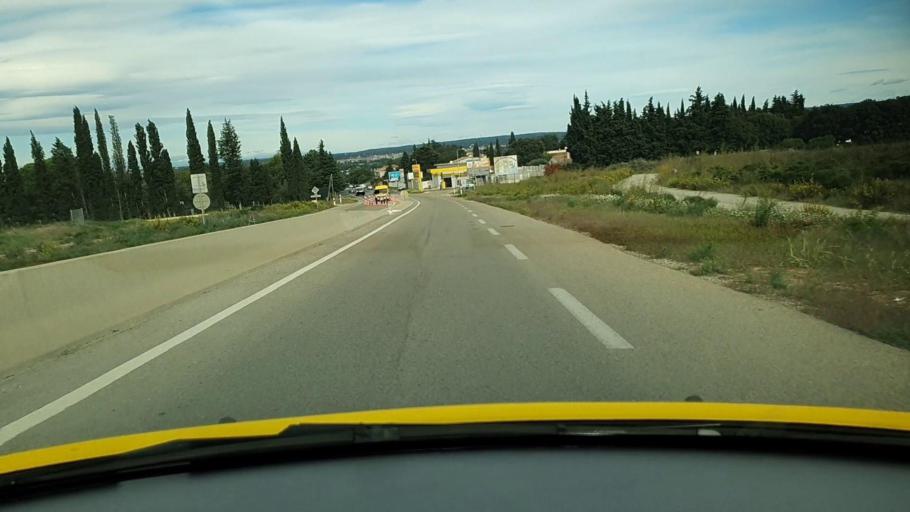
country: FR
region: Languedoc-Roussillon
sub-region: Departement du Gard
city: Caissargues
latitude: 43.7820
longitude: 4.3935
